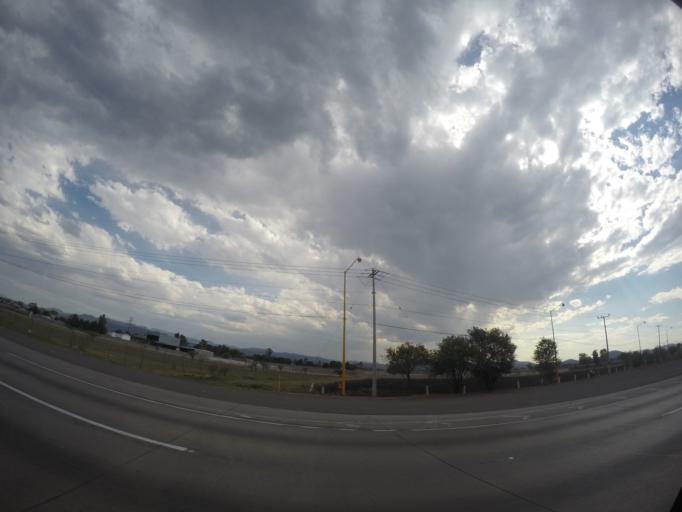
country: MX
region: Queretaro
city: La Estancia
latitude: 20.4133
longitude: -100.0412
